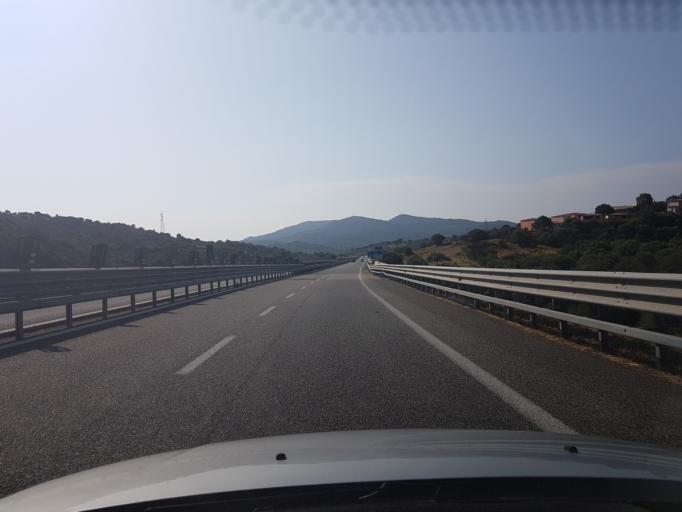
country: IT
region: Sardinia
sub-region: Provincia di Olbia-Tempio
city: San Teodoro
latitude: 40.7699
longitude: 9.6374
